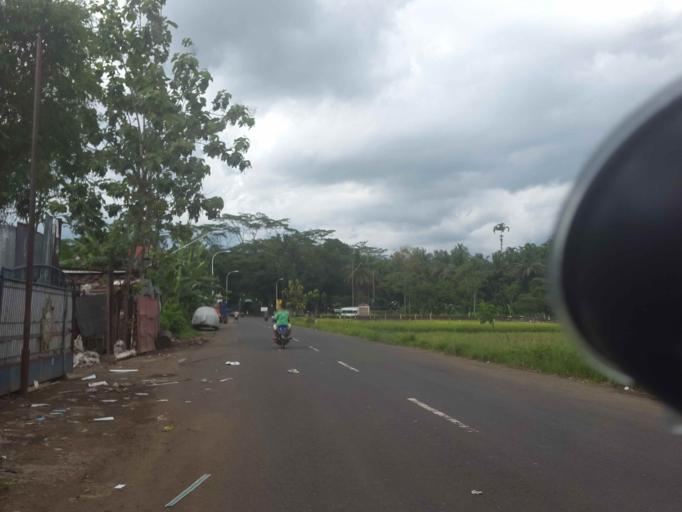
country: ID
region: Central Java
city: Purwokerto
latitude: -7.4190
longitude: 109.1960
